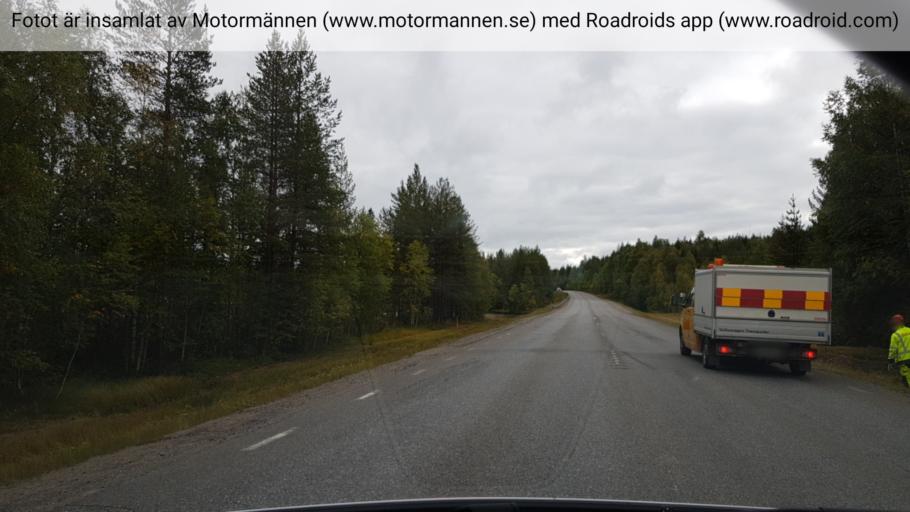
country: SE
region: Vaesterbotten
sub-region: Skelleftea Kommun
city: Boliden
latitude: 64.8949
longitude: 20.3742
